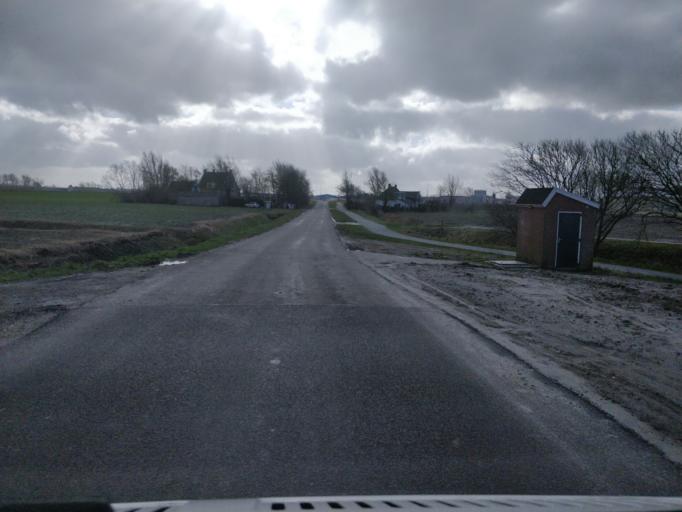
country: NL
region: Friesland
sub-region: Gemeente Harlingen
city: Harlingen
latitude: 53.1845
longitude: 5.4395
